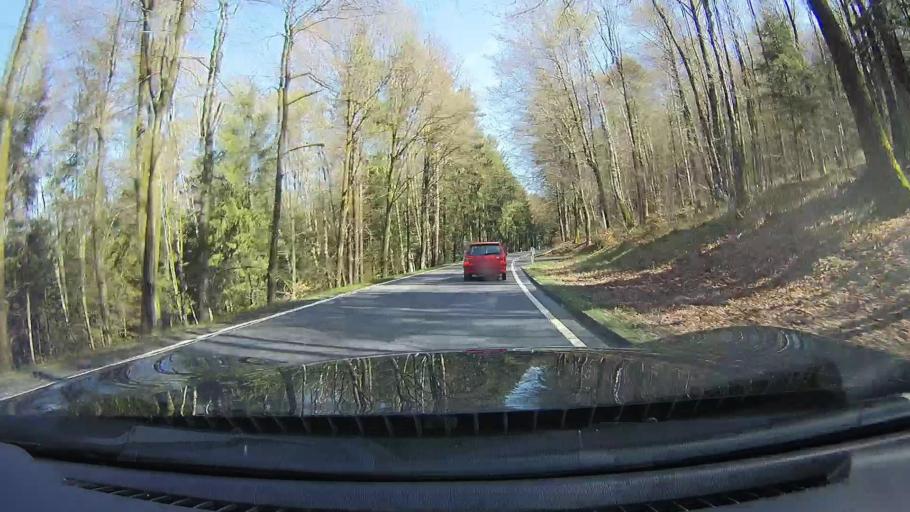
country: DE
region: Hesse
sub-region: Regierungsbezirk Darmstadt
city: Rothenberg
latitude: 49.5290
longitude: 8.9365
